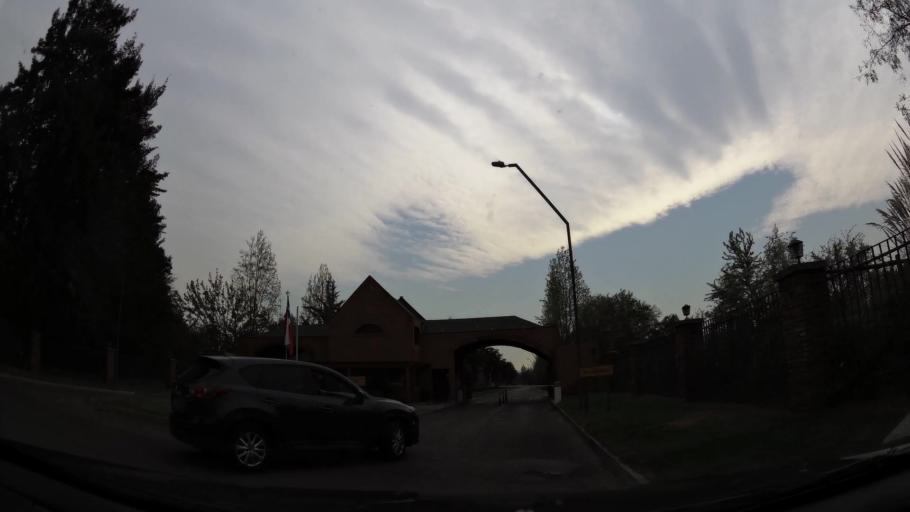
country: CL
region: Santiago Metropolitan
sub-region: Provincia de Chacabuco
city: Chicureo Abajo
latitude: -33.2762
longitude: -70.7052
